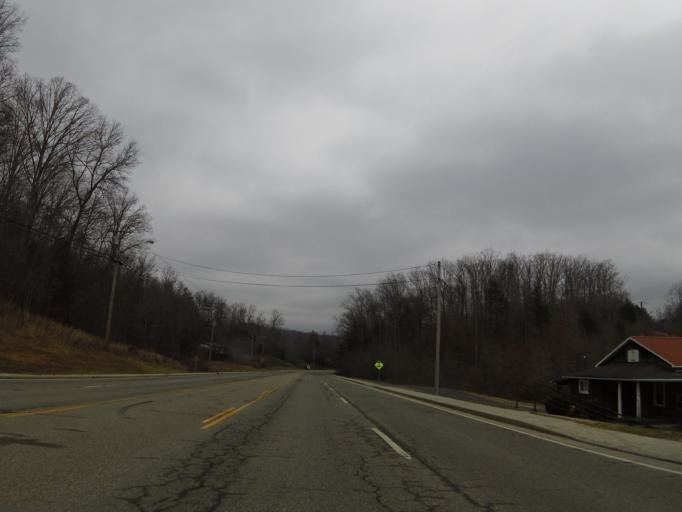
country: US
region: Tennessee
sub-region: Scott County
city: Huntsville
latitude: 36.4138
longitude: -84.5124
